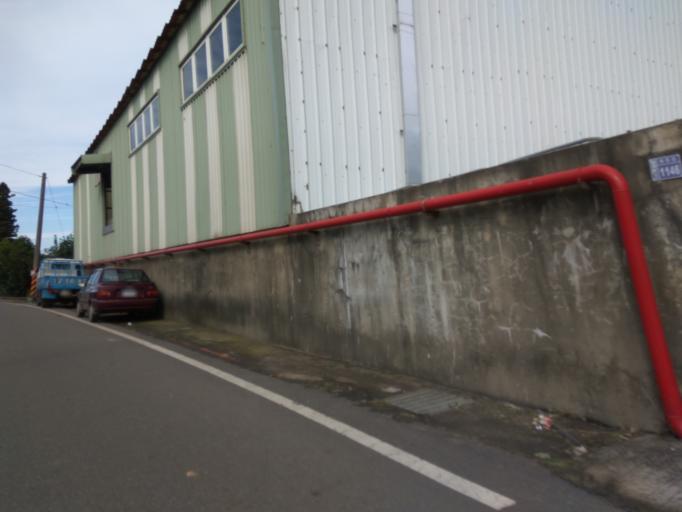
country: TW
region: Taiwan
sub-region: Hsinchu
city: Zhubei
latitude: 24.9608
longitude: 121.0998
